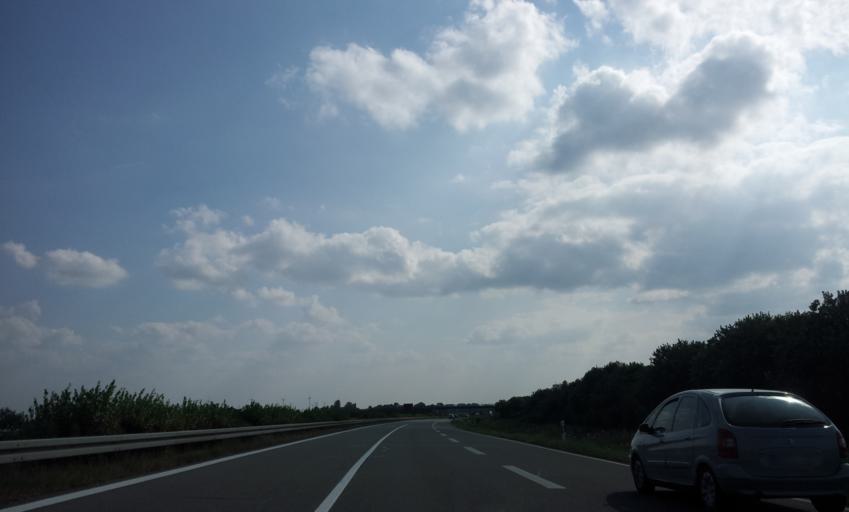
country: DE
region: Mecklenburg-Vorpommern
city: Jarmen
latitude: 53.9449
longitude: 13.3653
